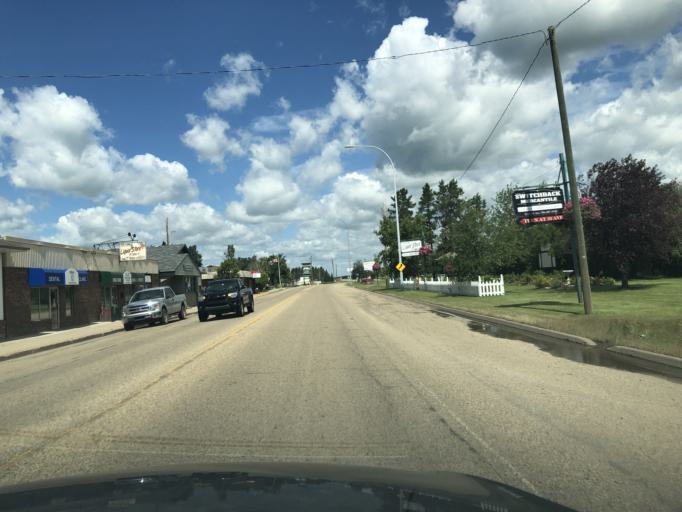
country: CA
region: Alberta
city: Millet
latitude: 53.0957
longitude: -113.4720
